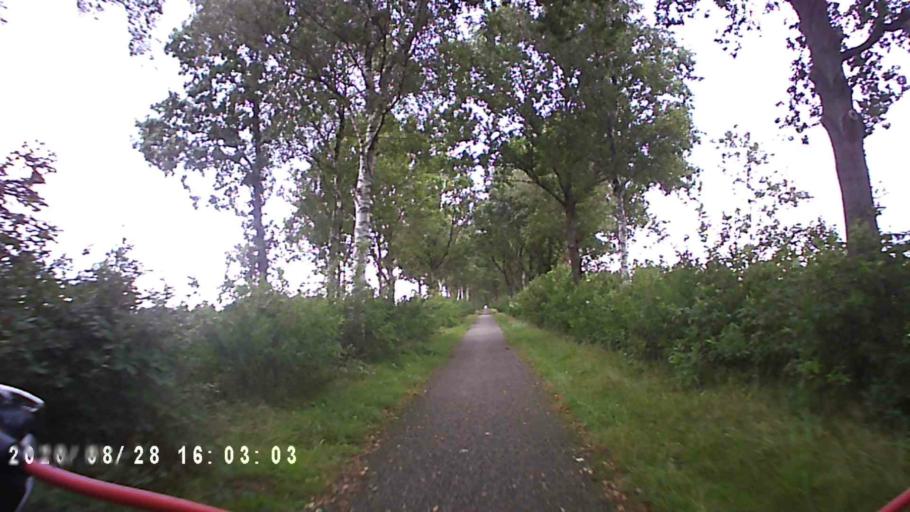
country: NL
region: Drenthe
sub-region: Gemeente Tynaarlo
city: Vries
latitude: 53.1090
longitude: 6.4990
